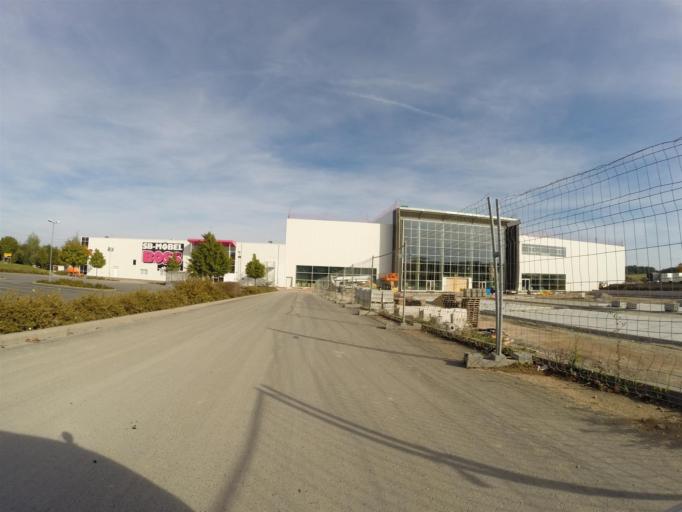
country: DE
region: Thuringia
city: Grossschwabhausen
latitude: 50.9594
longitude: 11.5112
